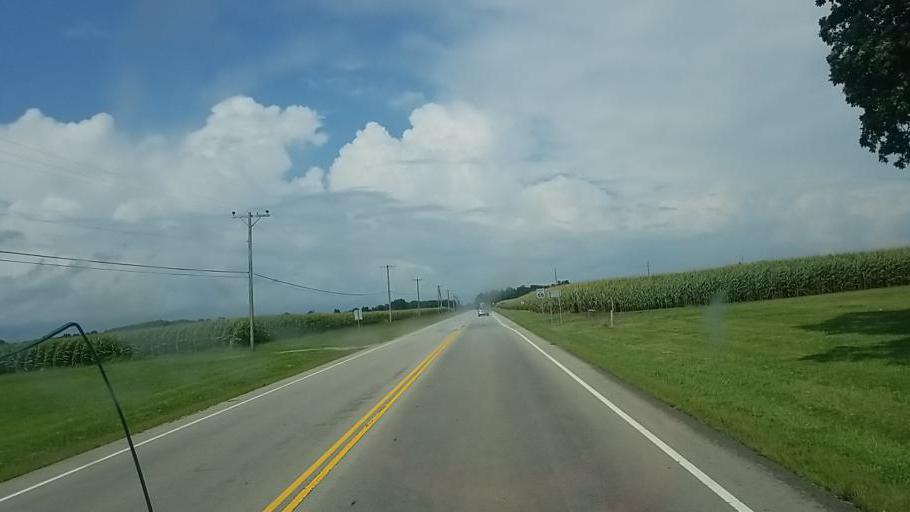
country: US
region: Ohio
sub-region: Champaign County
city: Urbana
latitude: 40.1366
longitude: -83.7476
